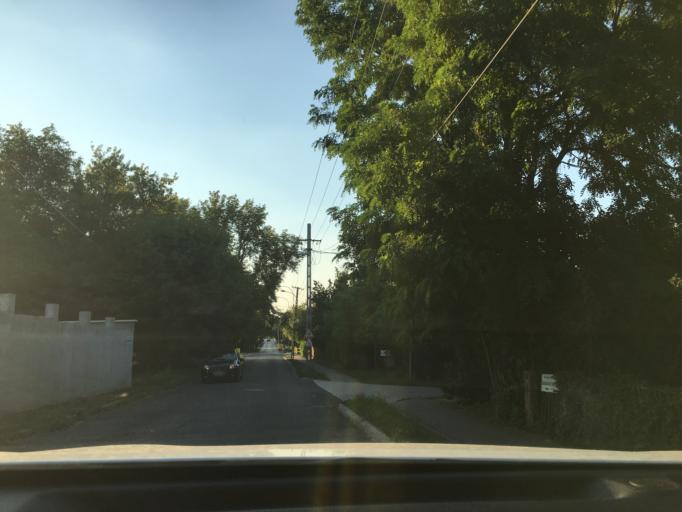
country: HU
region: Budapest
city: Budapest XVII. keruelet
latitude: 47.4840
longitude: 19.2729
